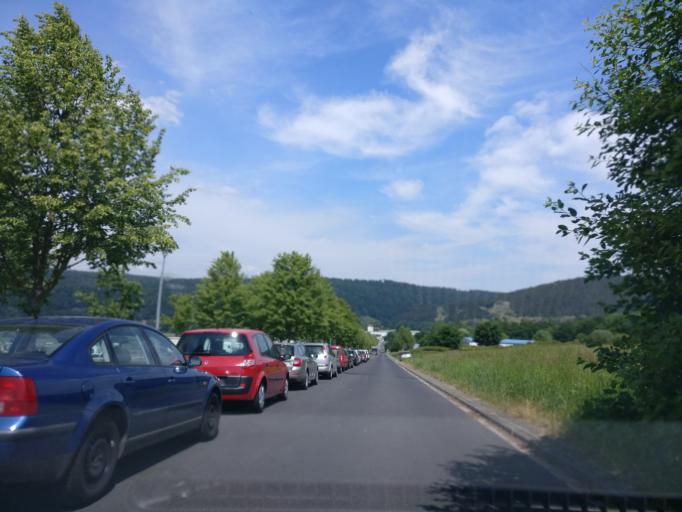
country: DE
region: Lower Saxony
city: Hannoversch Munden
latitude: 51.4333
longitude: 9.6551
